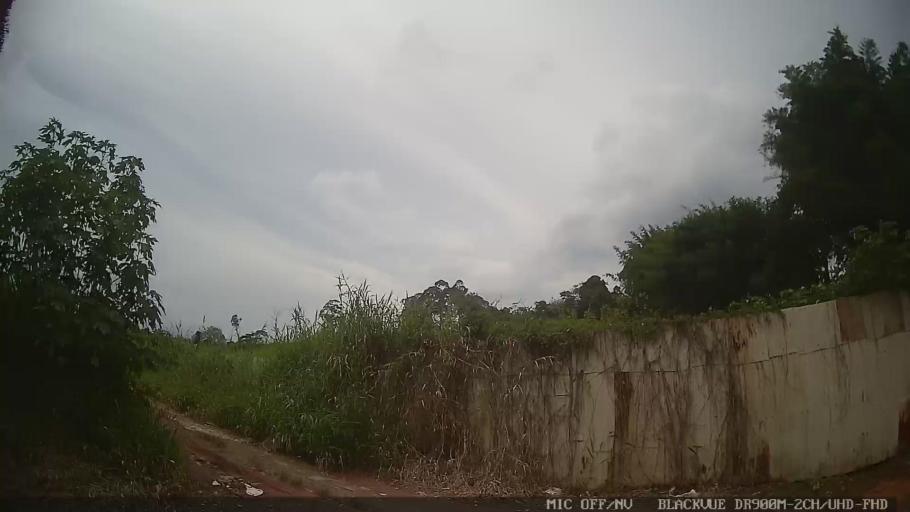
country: BR
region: Sao Paulo
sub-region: Itaquaquecetuba
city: Itaquaquecetuba
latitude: -23.4546
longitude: -46.3039
